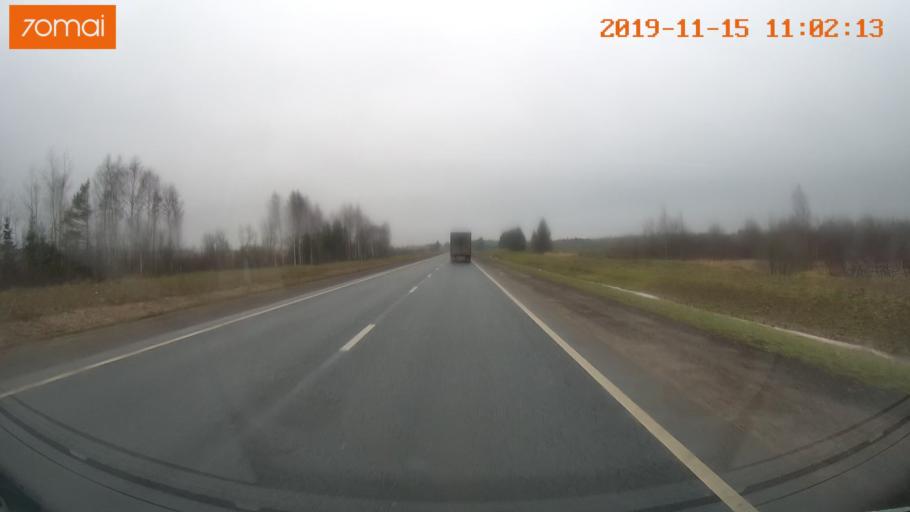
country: RU
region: Vologda
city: Chebsara
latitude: 59.1301
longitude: 38.9338
